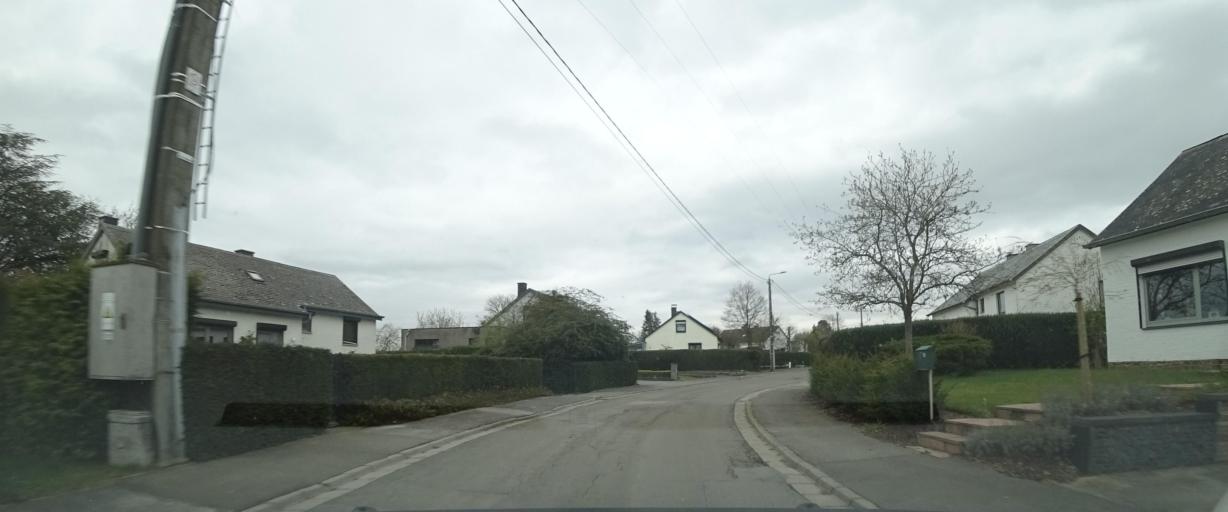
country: BE
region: Wallonia
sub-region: Province du Luxembourg
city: Marche-en-Famenne
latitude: 50.2216
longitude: 5.3509
